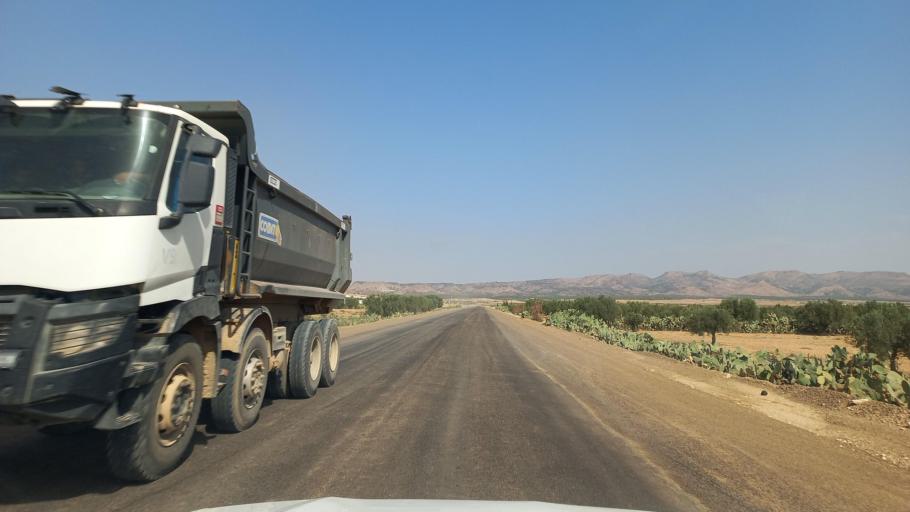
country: TN
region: Al Qasrayn
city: Sbiba
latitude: 35.3776
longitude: 9.0320
